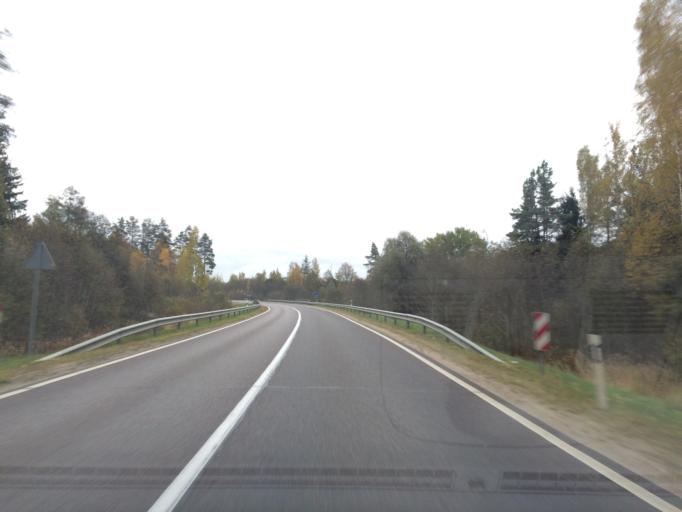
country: LV
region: Livani
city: Livani
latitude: 56.5328
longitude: 26.1401
